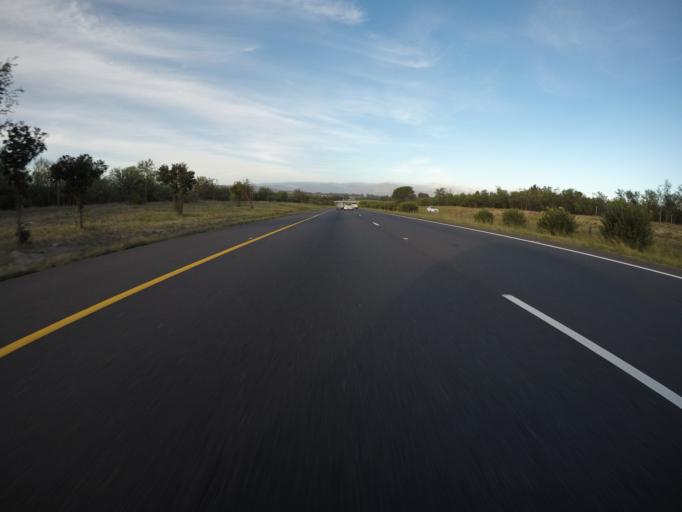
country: ZA
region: Western Cape
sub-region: Cape Winelands District Municipality
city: Stellenbosch
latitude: -33.8034
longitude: 18.8503
